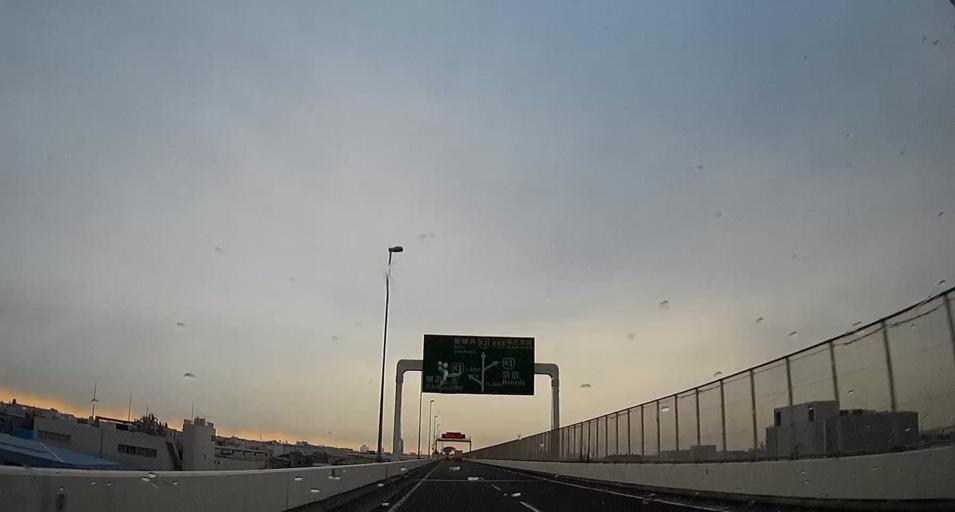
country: JP
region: Kanagawa
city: Yokohama
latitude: 35.4784
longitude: 139.6749
